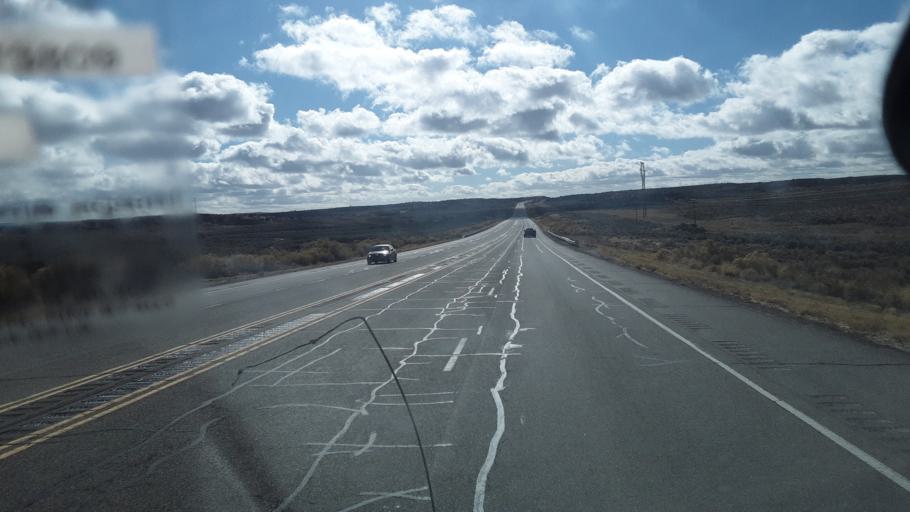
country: US
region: New Mexico
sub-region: San Juan County
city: Bloomfield
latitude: 36.3450
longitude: -107.7940
